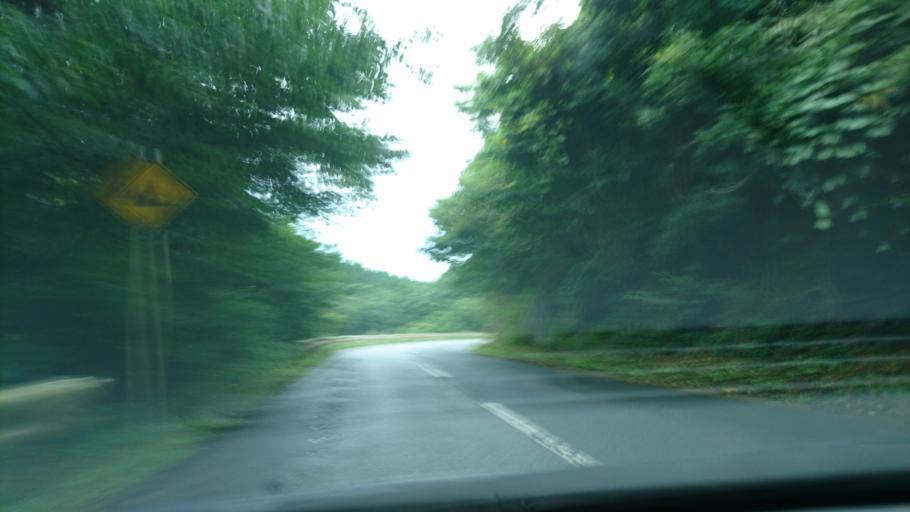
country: JP
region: Iwate
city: Mizusawa
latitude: 39.0379
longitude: 141.1923
